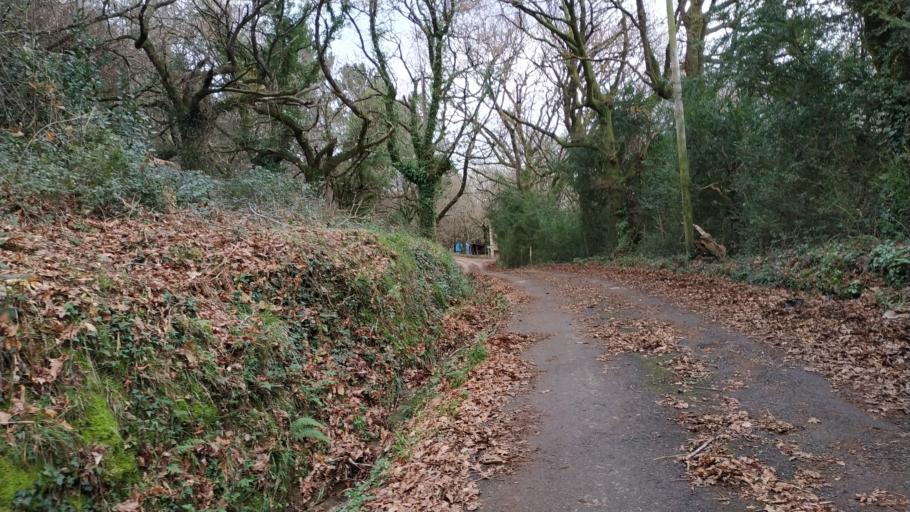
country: ES
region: Galicia
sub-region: Provincia de Pontevedra
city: Silleda
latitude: 42.7744
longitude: -8.1702
